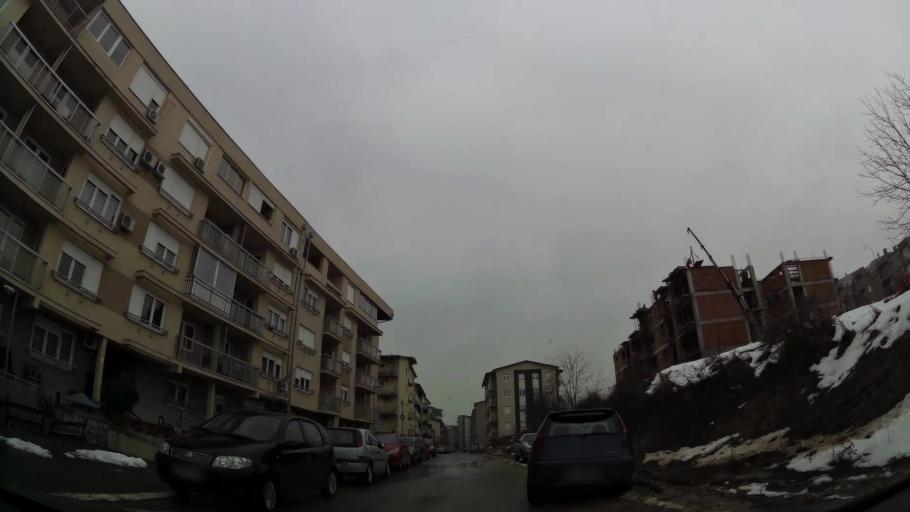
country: RS
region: Central Serbia
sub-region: Belgrade
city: Zvezdara
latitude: 44.7598
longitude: 20.5081
